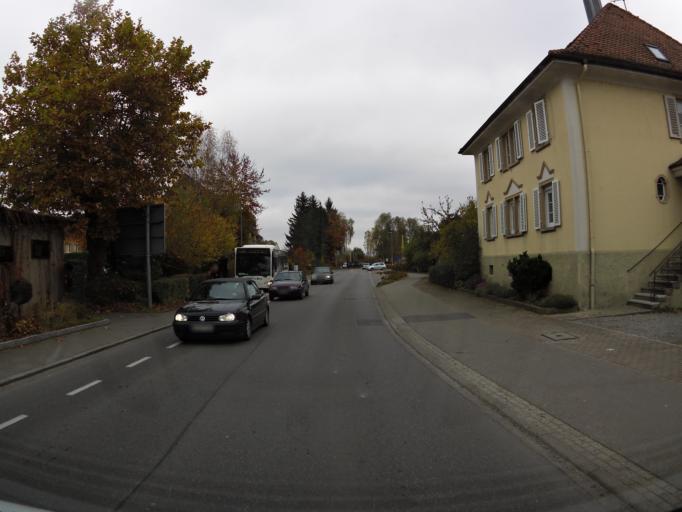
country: DE
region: Baden-Wuerttemberg
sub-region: Freiburg Region
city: Moos
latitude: 47.7262
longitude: 8.9344
